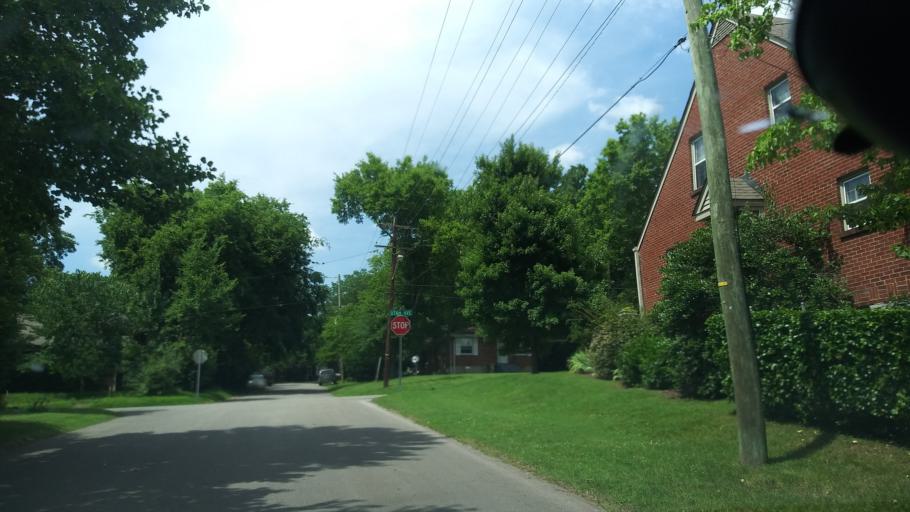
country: US
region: Tennessee
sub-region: Davidson County
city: Belle Meade
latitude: 36.1439
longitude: -86.8352
